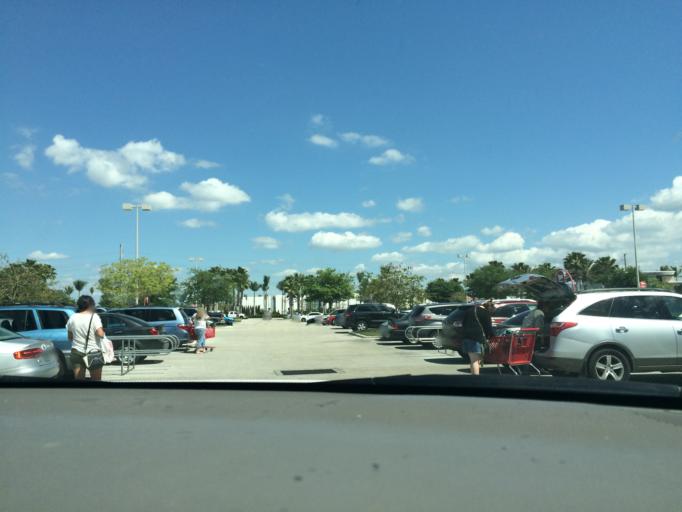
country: US
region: Florida
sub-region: Sarasota County
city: The Meadows
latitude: 27.3869
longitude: -82.4579
